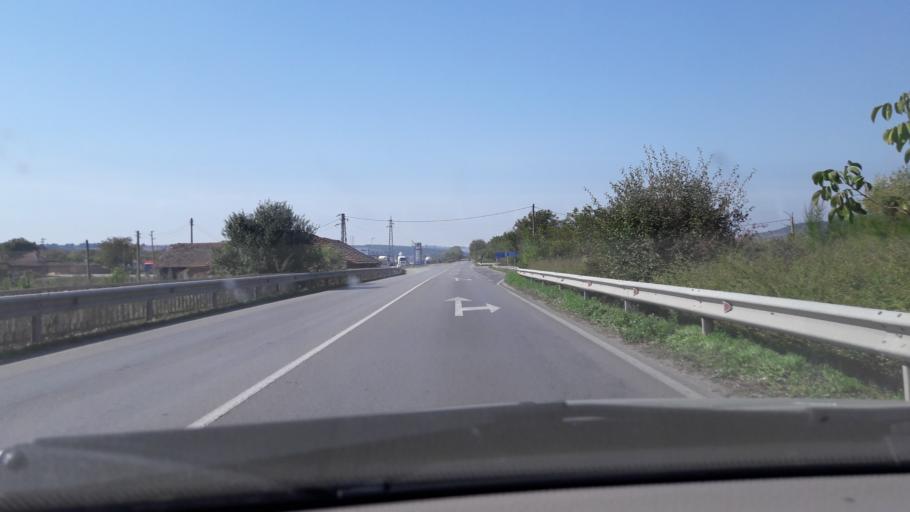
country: BG
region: Razgrad
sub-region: Obshtina Razgrad
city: Razgrad
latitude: 43.5481
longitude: 26.4806
